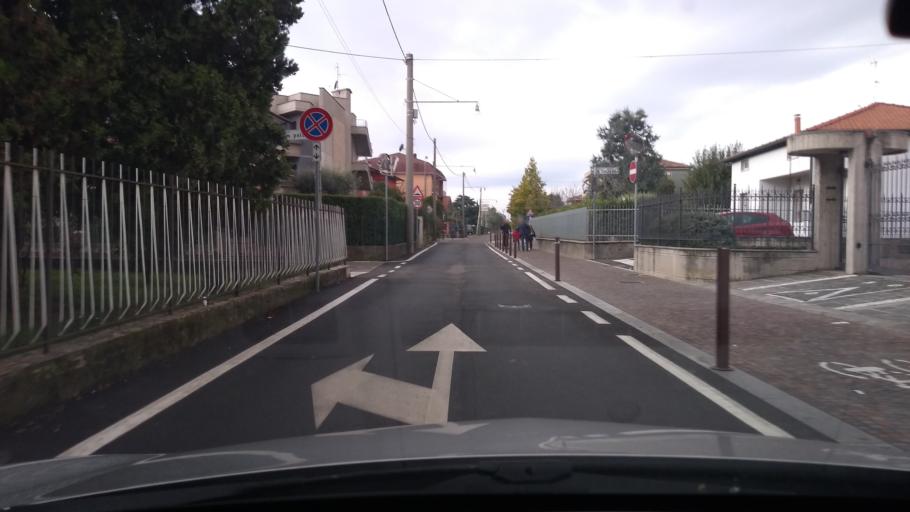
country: IT
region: Lombardy
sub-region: Provincia di Bergamo
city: Verdellino
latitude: 45.6026
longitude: 9.6130
